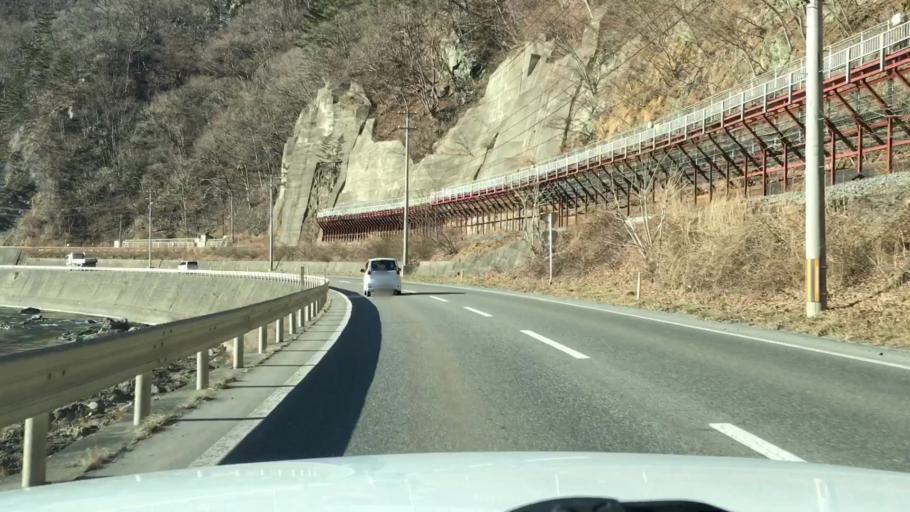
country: JP
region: Iwate
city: Miyako
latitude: 39.6105
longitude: 141.7771
